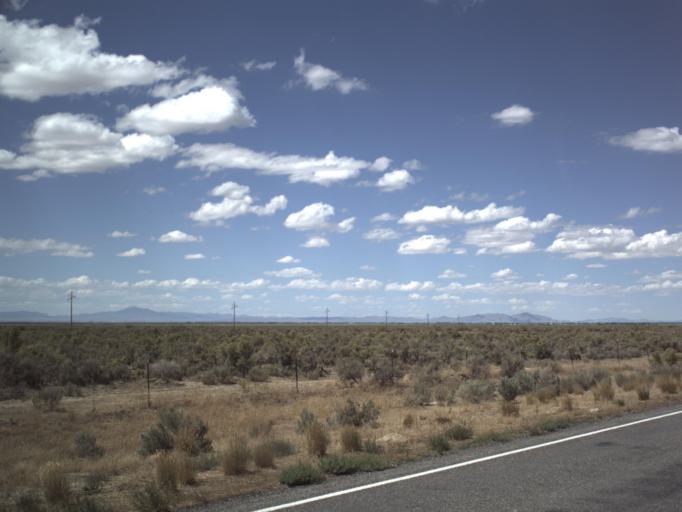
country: US
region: Utah
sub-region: Millard County
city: Delta
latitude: 39.2279
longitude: -112.4252
